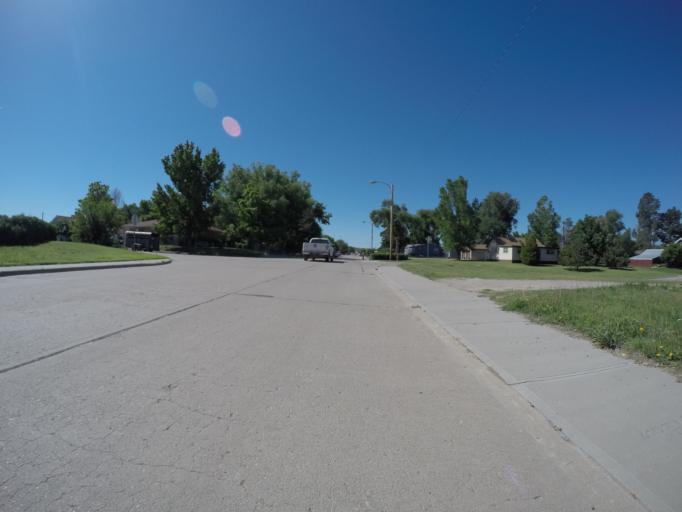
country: US
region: Kansas
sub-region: Rawlins County
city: Atwood
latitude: 39.8115
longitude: -101.0423
